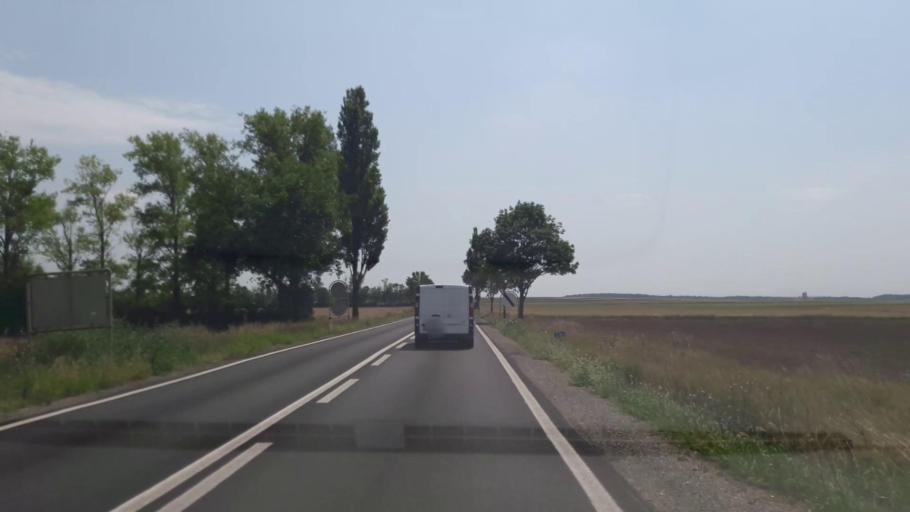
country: AT
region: Lower Austria
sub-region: Politischer Bezirk Wien-Umgebung
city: Rauchenwarth
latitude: 48.1050
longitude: 16.5318
